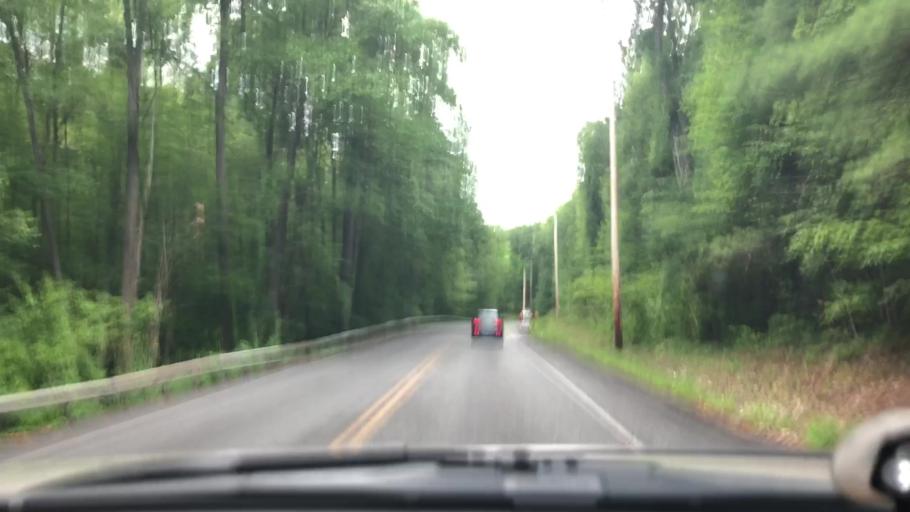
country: US
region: New York
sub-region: Saratoga County
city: Corinth
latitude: 43.1909
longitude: -73.7536
